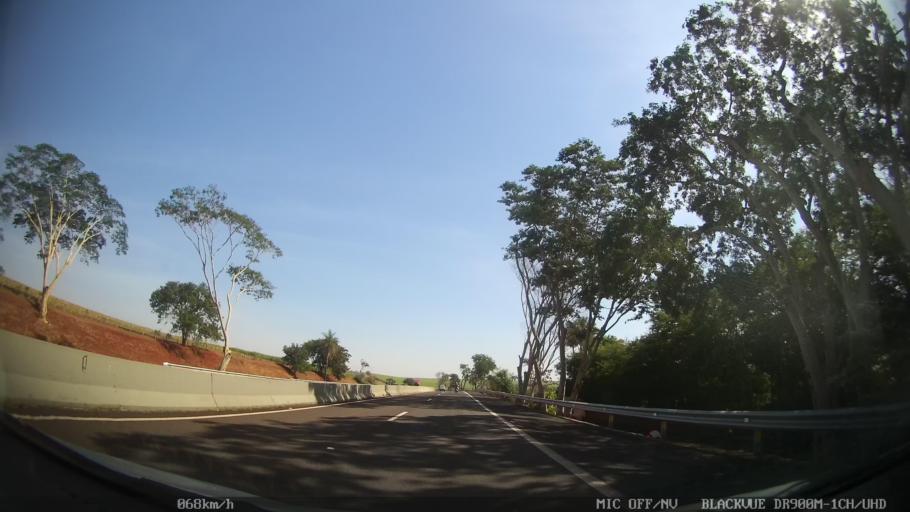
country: BR
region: Sao Paulo
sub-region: Ribeirao Preto
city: Ribeirao Preto
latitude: -21.1664
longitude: -47.8749
